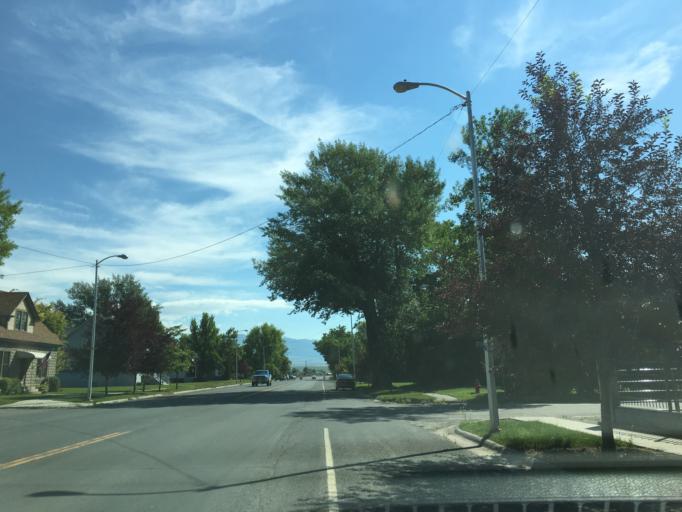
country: US
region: Montana
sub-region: Broadwater County
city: Townsend
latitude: 46.3216
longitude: -111.5138
